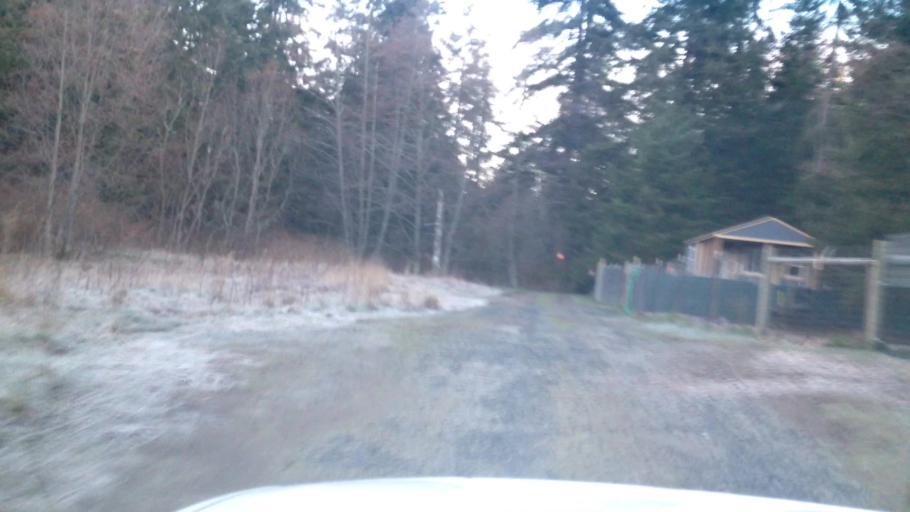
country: US
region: Washington
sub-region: Island County
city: Coupeville
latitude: 48.1796
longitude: -122.6129
